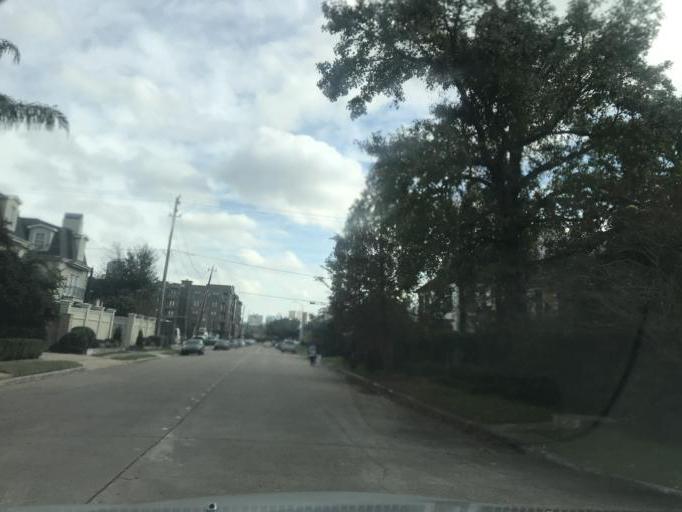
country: US
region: Texas
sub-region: Harris County
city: Hunters Creek Village
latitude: 29.7459
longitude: -95.4871
